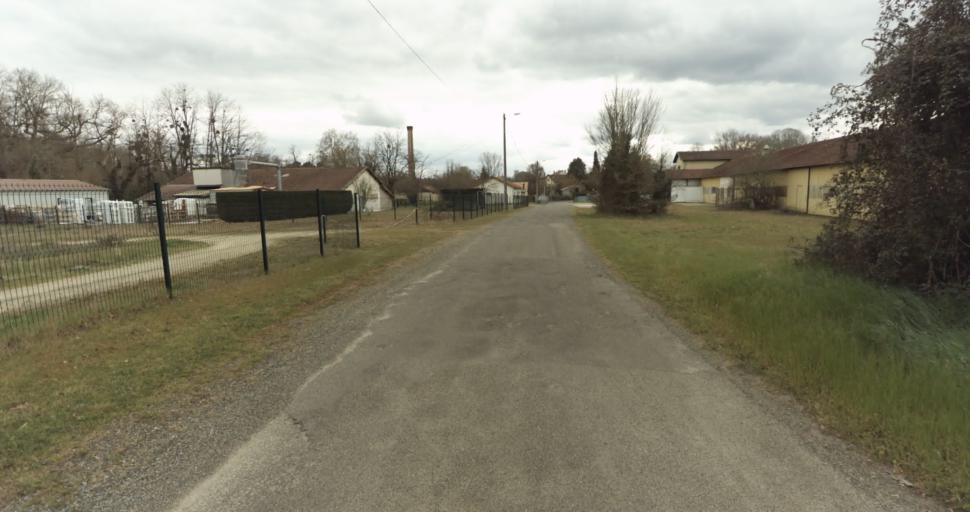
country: FR
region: Aquitaine
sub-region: Departement des Landes
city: Roquefort
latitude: 44.0404
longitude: -0.3211
